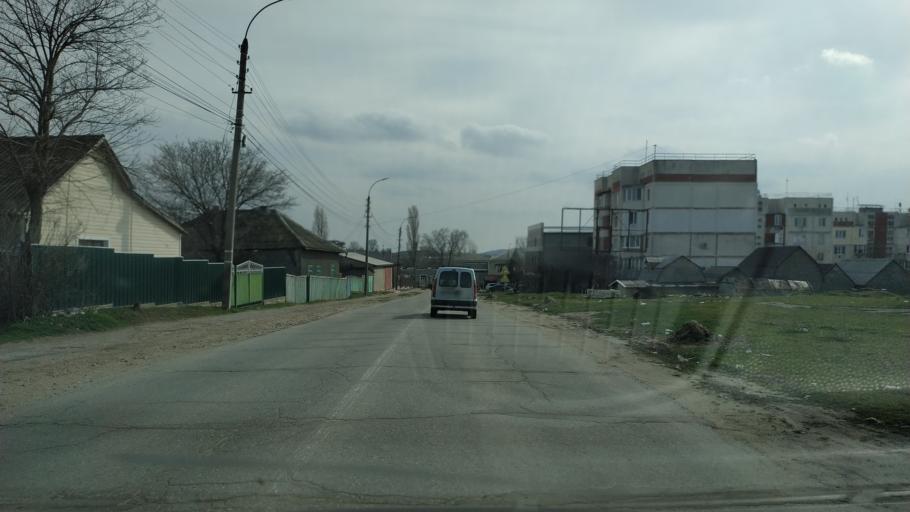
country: MD
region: Gagauzia
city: Vulcanesti
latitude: 45.6897
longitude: 28.4062
